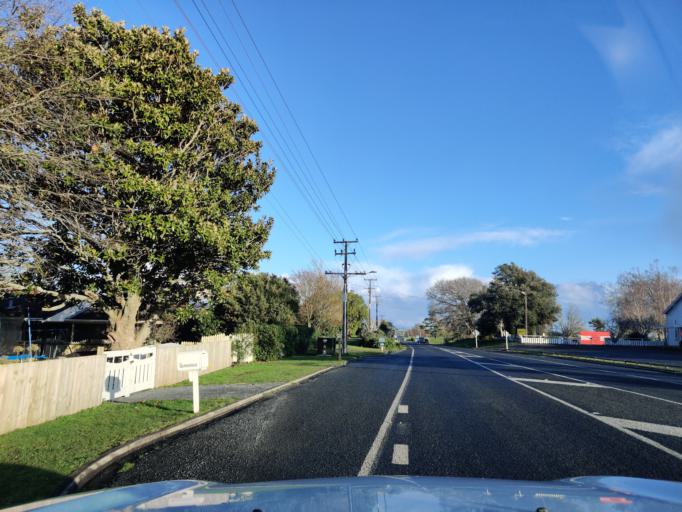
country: NZ
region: Waikato
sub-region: Hauraki District
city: Paeroa
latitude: -37.5896
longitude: 175.5023
